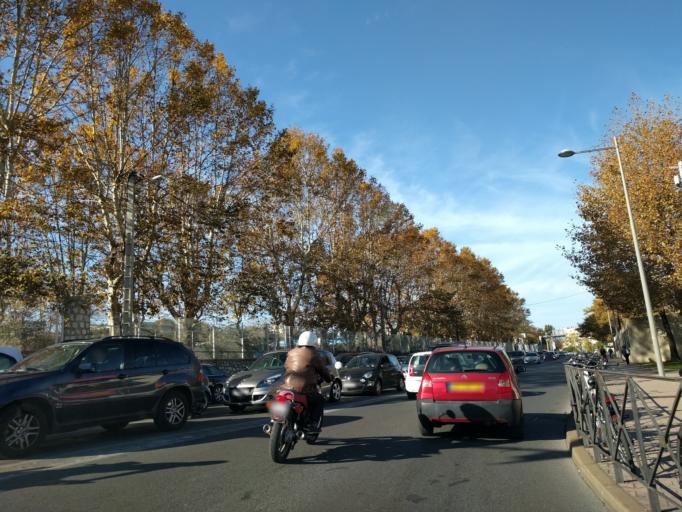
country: FR
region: Languedoc-Roussillon
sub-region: Departement de l'Herault
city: Montpellier
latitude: 43.6106
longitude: 3.8905
